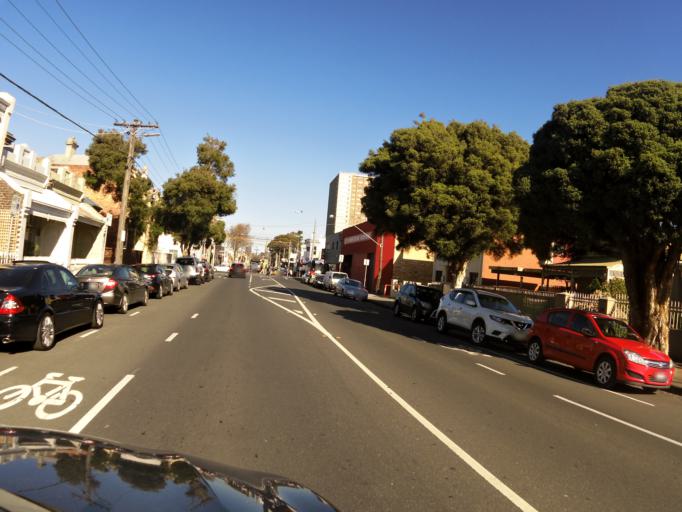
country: AU
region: Victoria
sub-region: Yarra
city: Richmond
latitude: -37.8098
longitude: 145.0007
